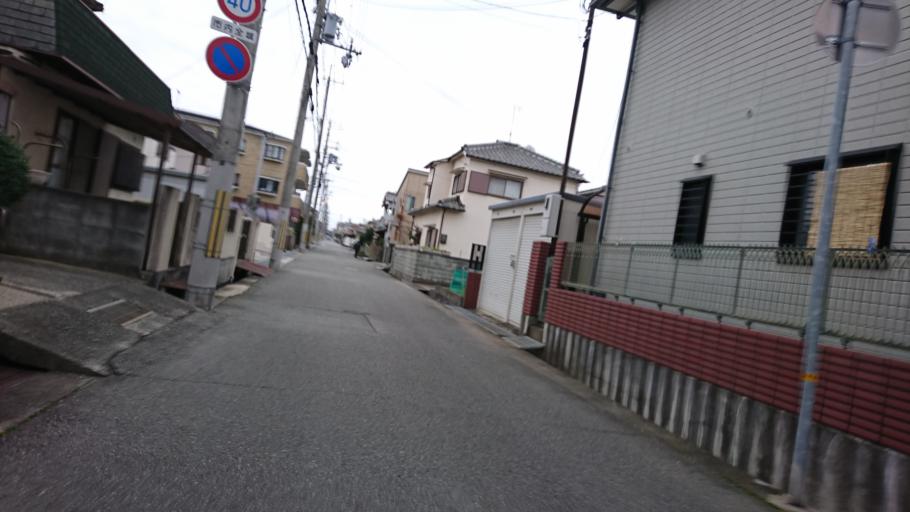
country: JP
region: Hyogo
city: Kakogawacho-honmachi
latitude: 34.7470
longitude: 134.8605
